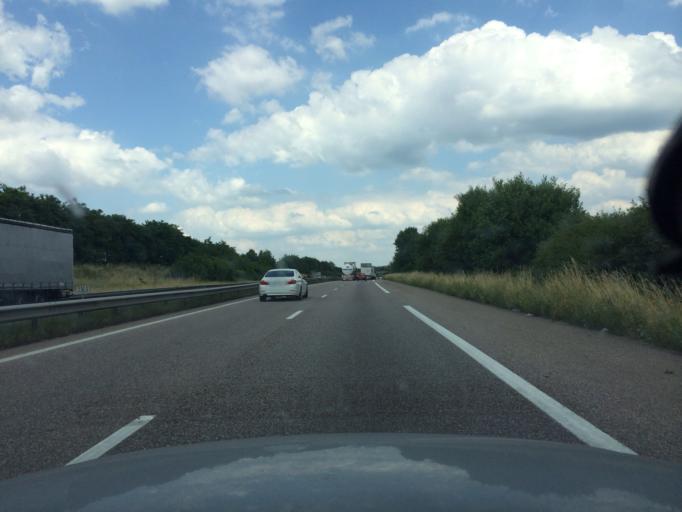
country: FR
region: Lorraine
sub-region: Departement de Meurthe-et-Moselle
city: Gondreville
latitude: 48.6864
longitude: 5.9571
